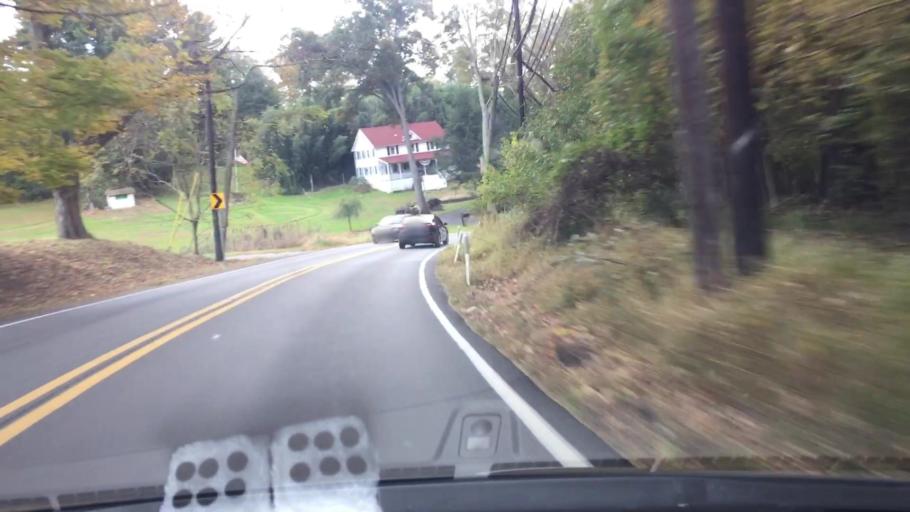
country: US
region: Pennsylvania
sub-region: Delaware County
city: Media
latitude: 39.9206
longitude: -75.4042
